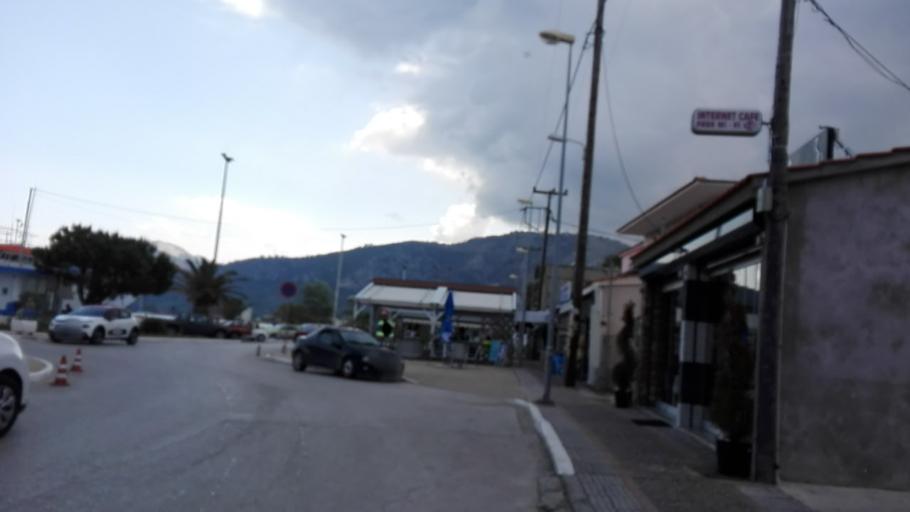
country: GR
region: East Macedonia and Thrace
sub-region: Nomos Kavalas
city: Prinos
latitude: 40.7586
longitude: 24.5759
